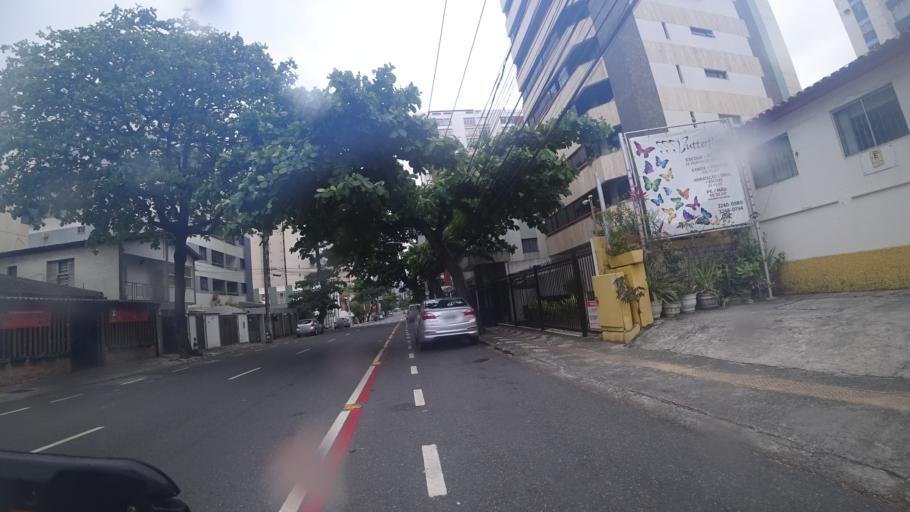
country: BR
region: Bahia
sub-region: Salvador
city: Salvador
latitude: -13.0027
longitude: -38.4557
